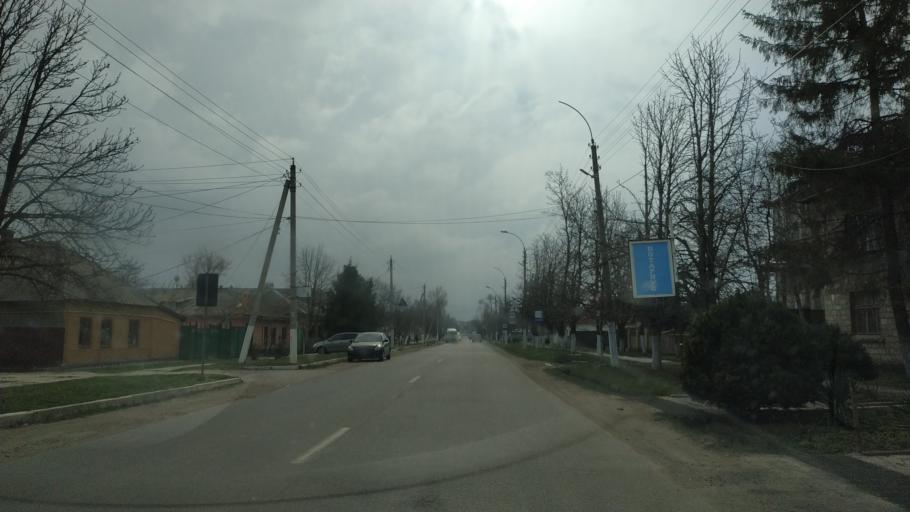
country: MD
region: Basarabeasca
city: Basarabeasca
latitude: 46.3362
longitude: 28.9587
